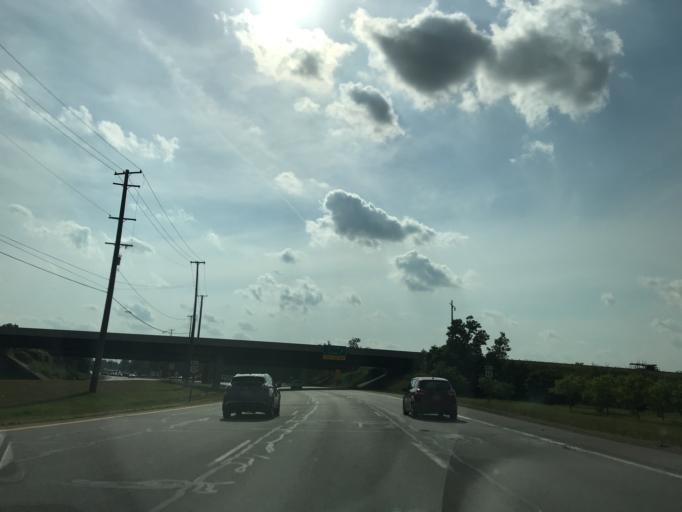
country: US
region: Michigan
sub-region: Wayne County
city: Canton
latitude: 42.2804
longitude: -83.4395
